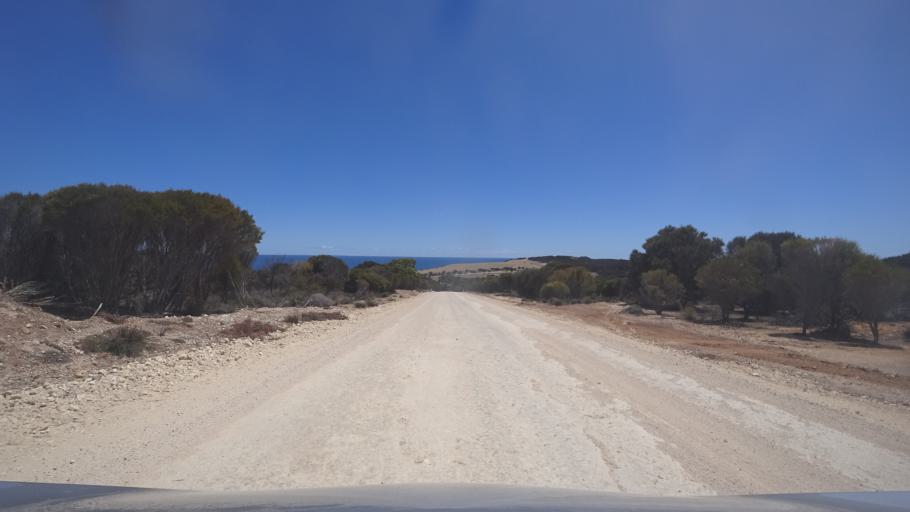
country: AU
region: South Australia
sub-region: Kangaroo Island
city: Kingscote
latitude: -35.6287
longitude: 137.2128
